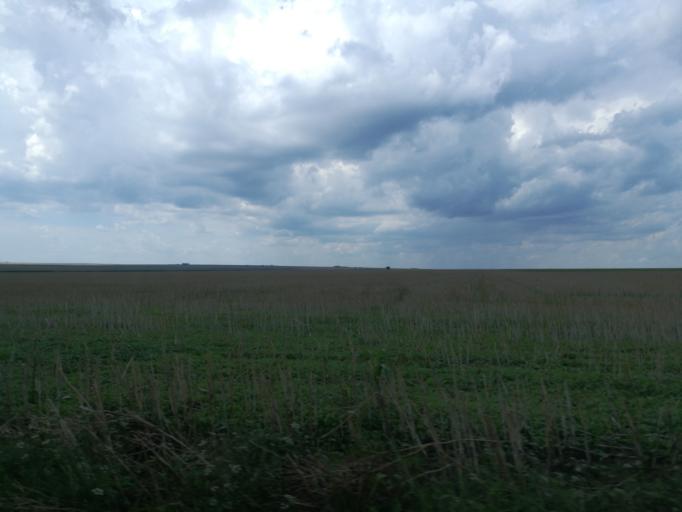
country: RO
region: Constanta
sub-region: Comuna Corbu
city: Corbu
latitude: 44.4240
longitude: 28.6753
